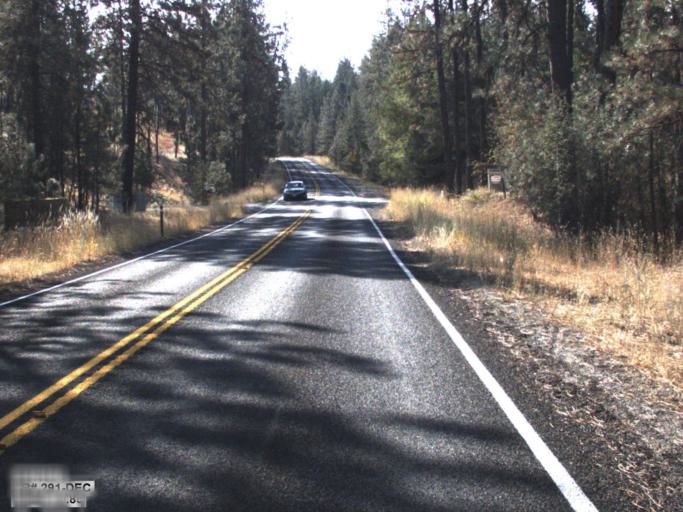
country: US
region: Washington
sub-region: Spokane County
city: Deer Park
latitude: 47.8785
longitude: -117.6560
